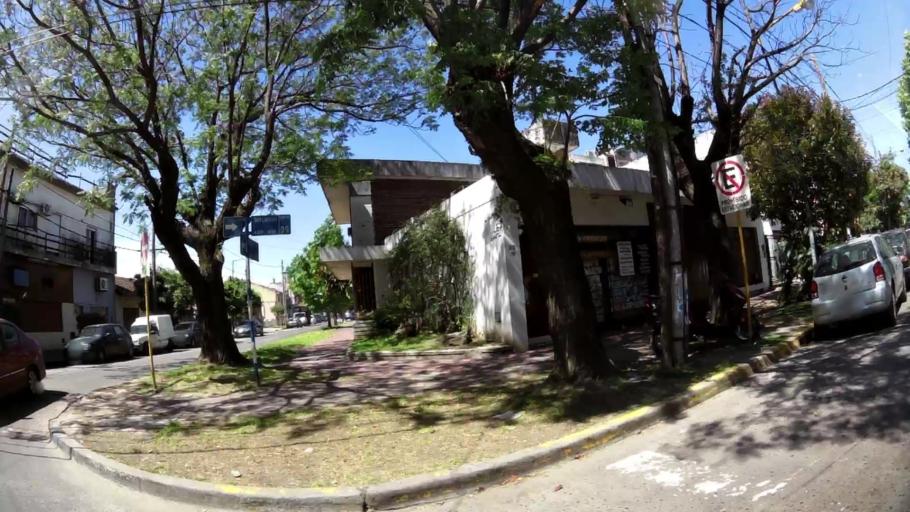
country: AR
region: Buenos Aires
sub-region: Partido de General San Martin
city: General San Martin
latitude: -34.5625
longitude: -58.5597
